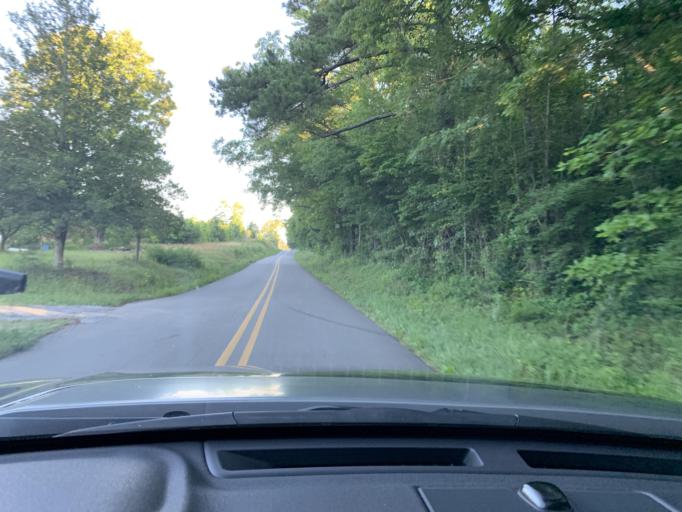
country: US
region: Georgia
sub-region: Bartow County
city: Rydal
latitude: 34.2577
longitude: -84.6943
